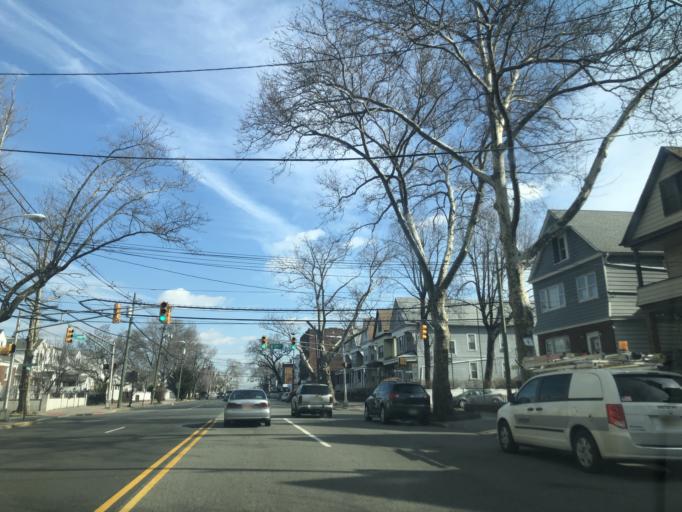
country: US
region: New Jersey
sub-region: Hudson County
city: Bayonne
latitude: 40.6610
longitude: -74.1273
